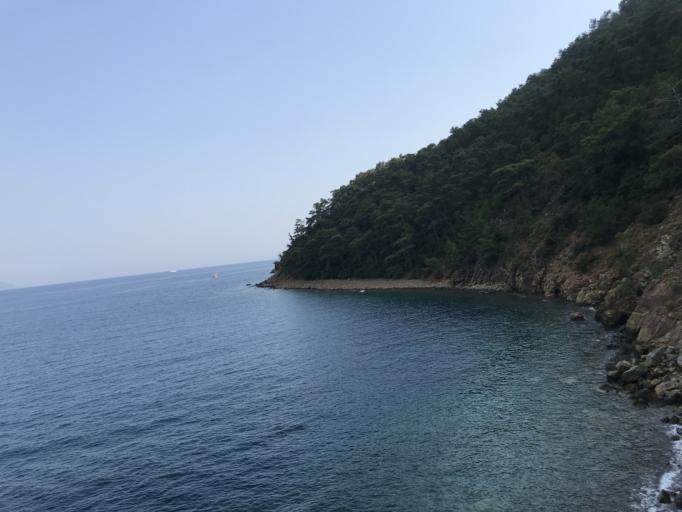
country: TR
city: Dalyan
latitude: 36.8273
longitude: 28.5498
